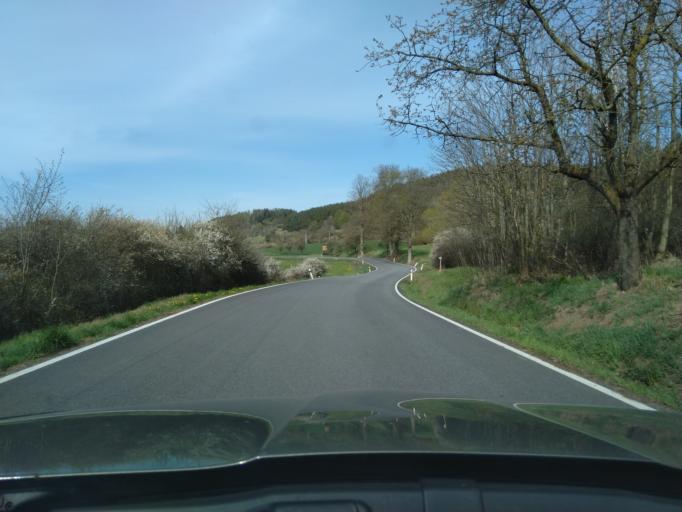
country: CZ
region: Jihocesky
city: Ckyne
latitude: 49.1179
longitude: 13.8102
